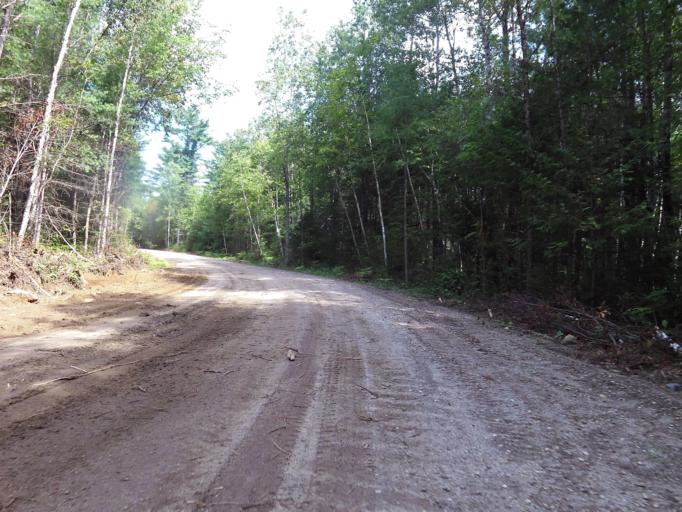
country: CA
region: Ontario
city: Renfrew
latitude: 45.1118
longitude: -76.7245
